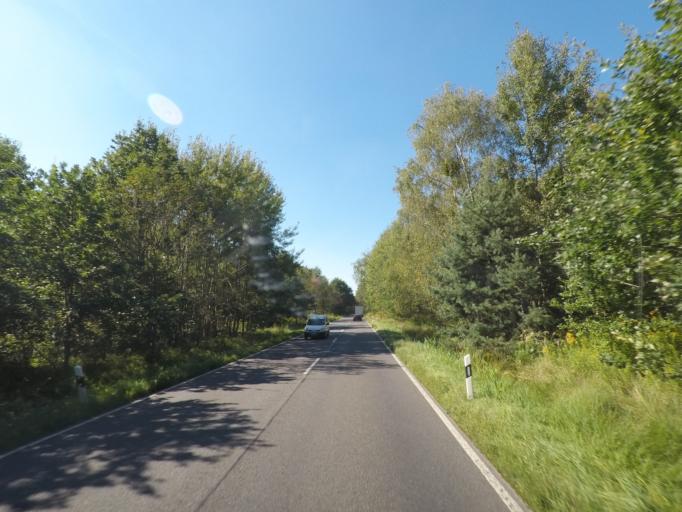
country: DE
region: Brandenburg
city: Welzow
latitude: 51.5621
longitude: 14.1190
